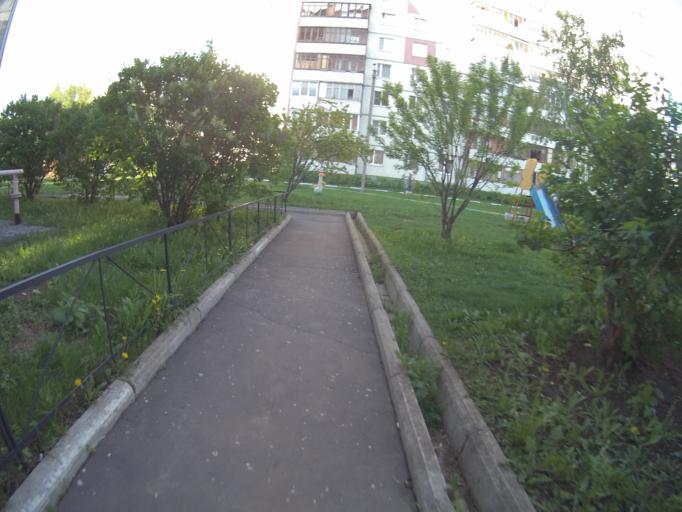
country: RU
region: Vladimir
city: Kommunar
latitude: 56.1707
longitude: 40.4502
